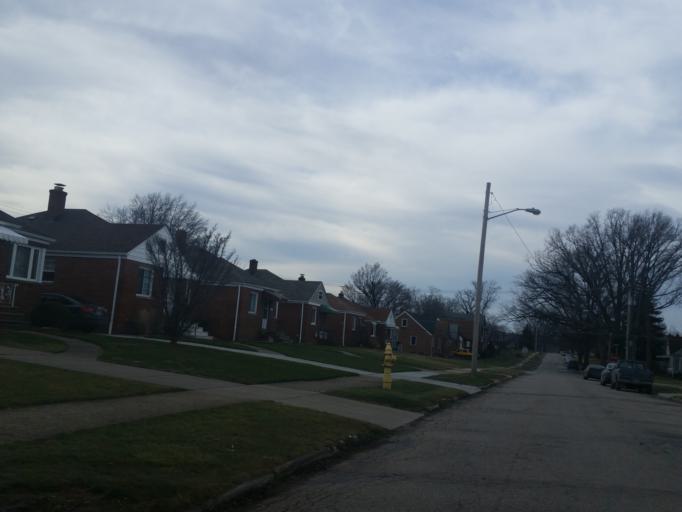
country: US
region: Ohio
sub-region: Cuyahoga County
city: Brooklyn Heights
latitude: 41.4133
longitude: -81.6973
